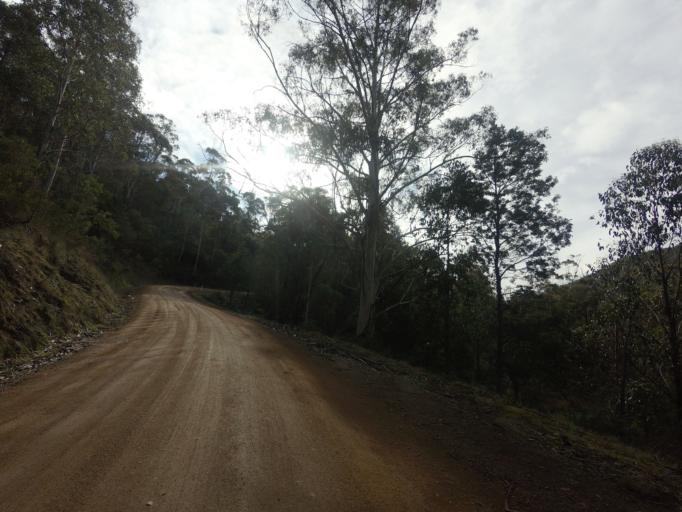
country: AU
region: Tasmania
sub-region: Derwent Valley
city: New Norfolk
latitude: -42.7892
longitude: 146.9413
